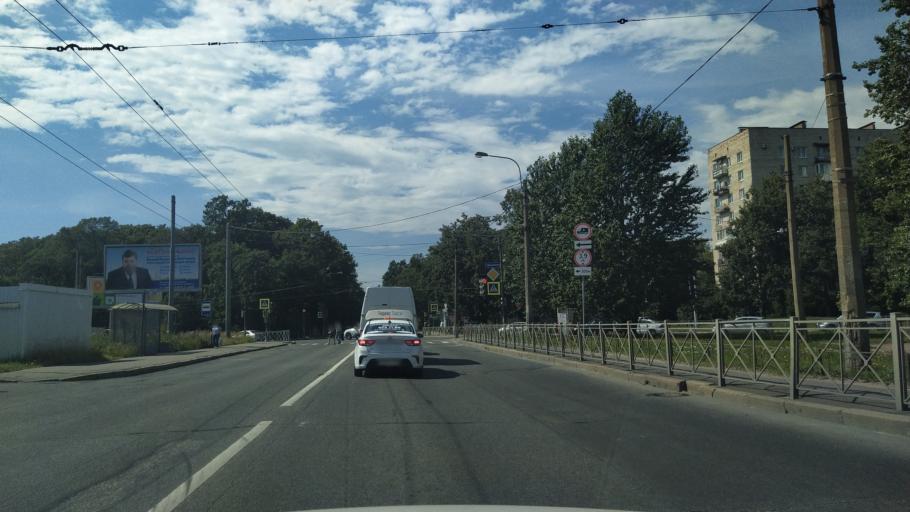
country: RU
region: St.-Petersburg
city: Kushelevka
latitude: 59.9944
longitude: 30.3559
